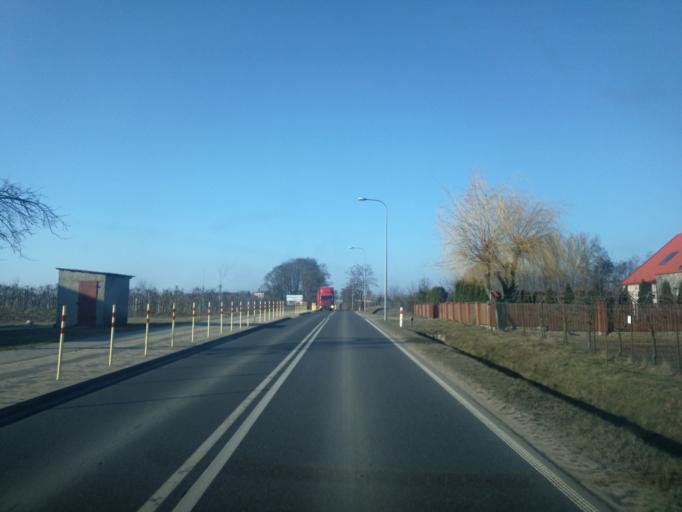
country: PL
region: Warmian-Masurian Voivodeship
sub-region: Powiat ilawski
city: Lubawa
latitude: 53.4591
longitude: 19.7767
